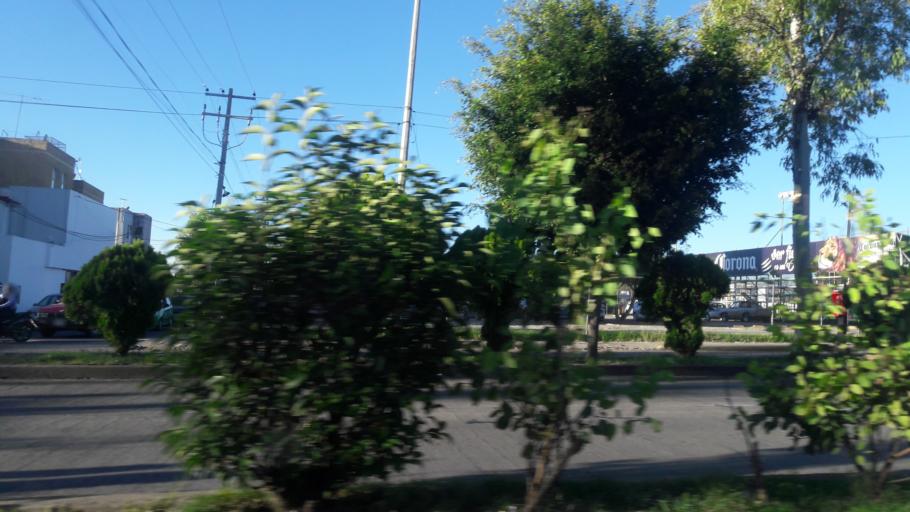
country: MX
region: Guanajuato
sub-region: Leon
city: La Ermita
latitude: 21.1461
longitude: -101.7004
